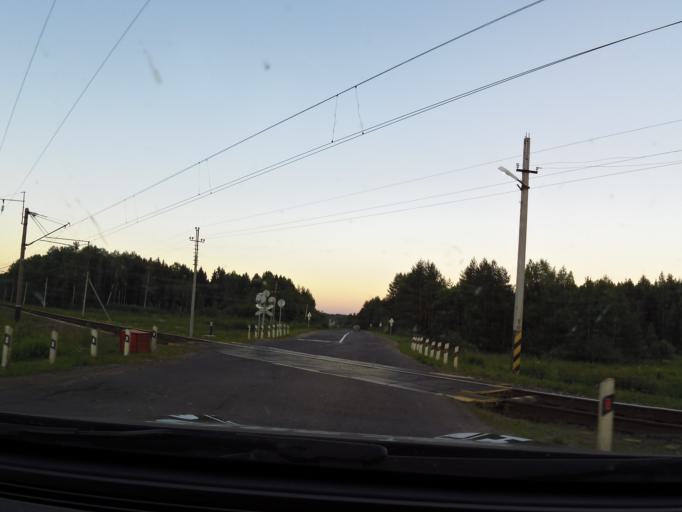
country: RU
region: Jaroslavl
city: Lyubim
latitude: 58.3340
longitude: 40.8923
